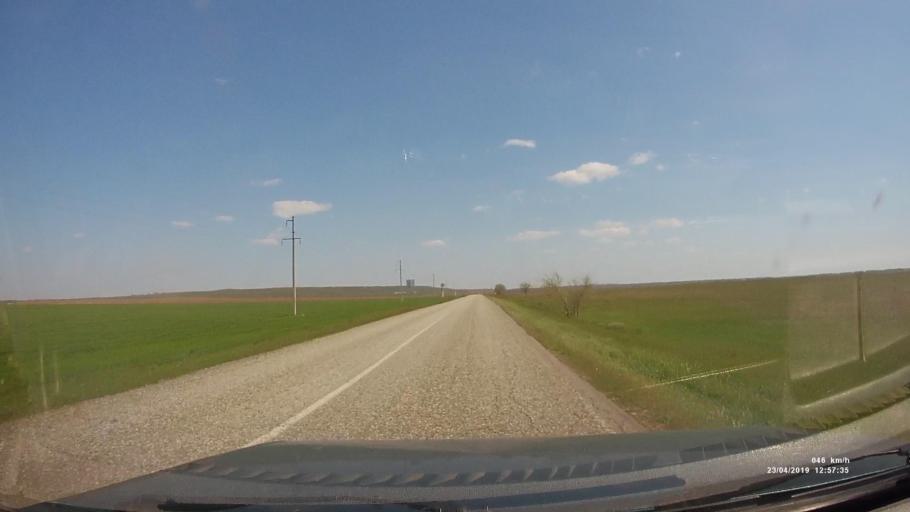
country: RU
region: Kalmykiya
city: Yashalta
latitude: 46.6039
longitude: 42.5818
